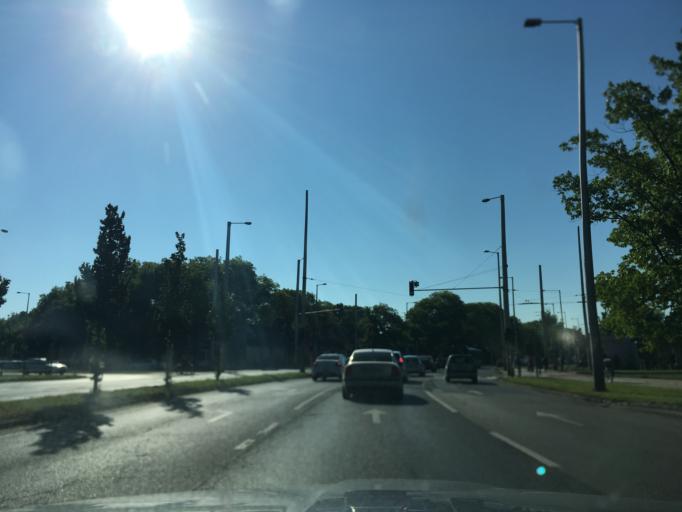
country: HU
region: Hajdu-Bihar
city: Debrecen
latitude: 47.5294
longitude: 21.6125
